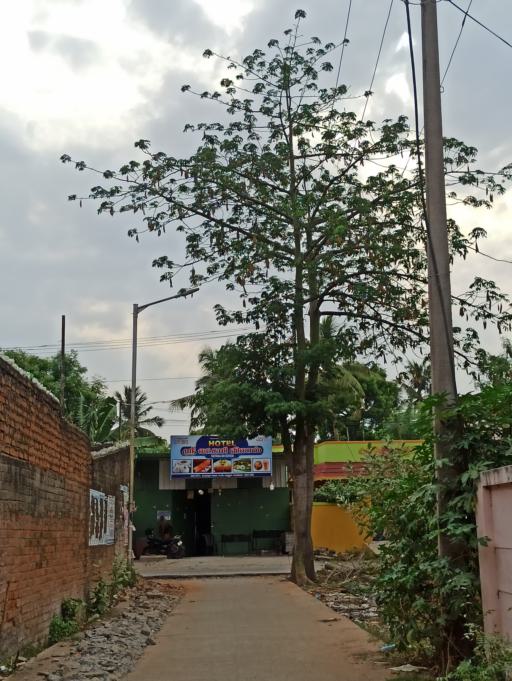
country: IN
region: Tamil Nadu
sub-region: Thiruvallur
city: Chinnasekkadu
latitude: 13.1683
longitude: 80.2391
